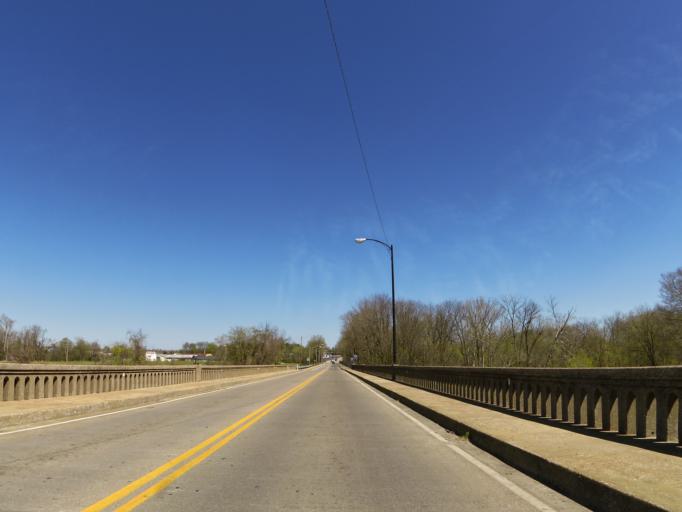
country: US
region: Kentucky
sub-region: Warren County
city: Bowling Green
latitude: 37.0003
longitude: -86.4290
